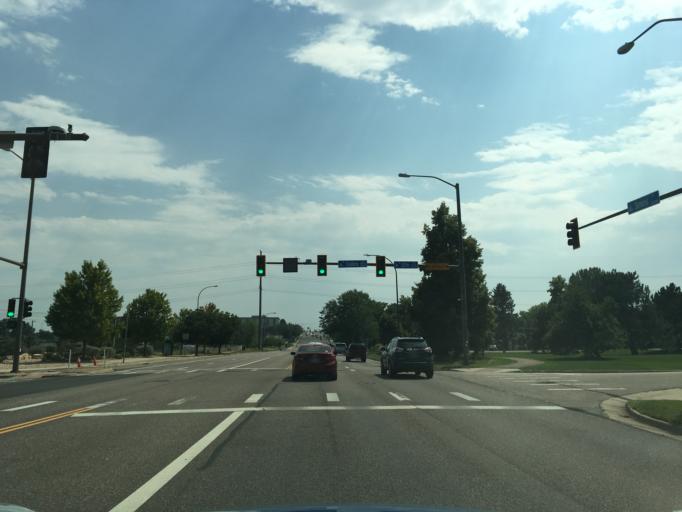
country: US
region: Colorado
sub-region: Jefferson County
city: Applewood
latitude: 39.7349
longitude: -105.1285
